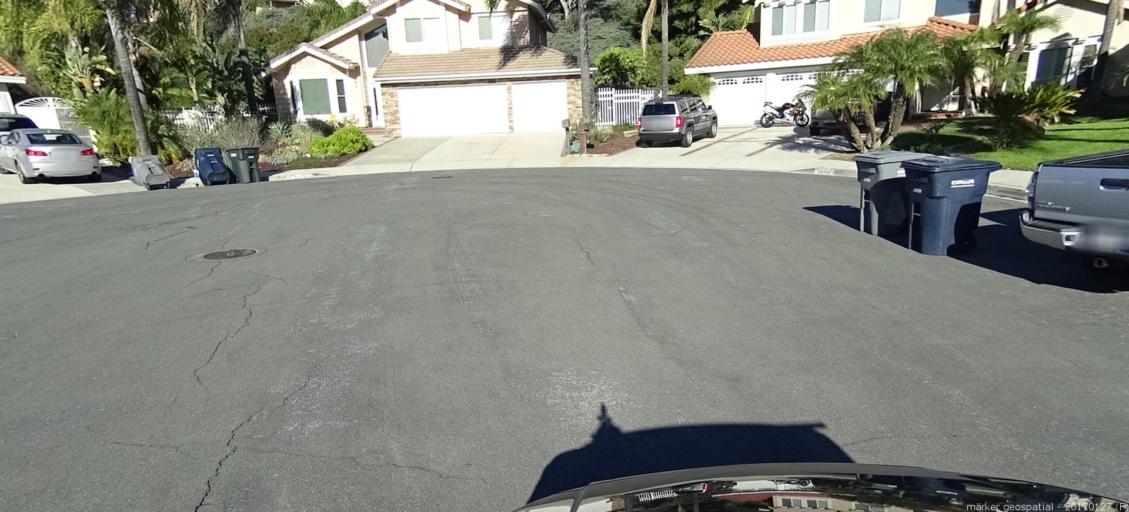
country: US
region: California
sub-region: Orange County
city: Lake Forest
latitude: 33.6527
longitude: -117.6696
